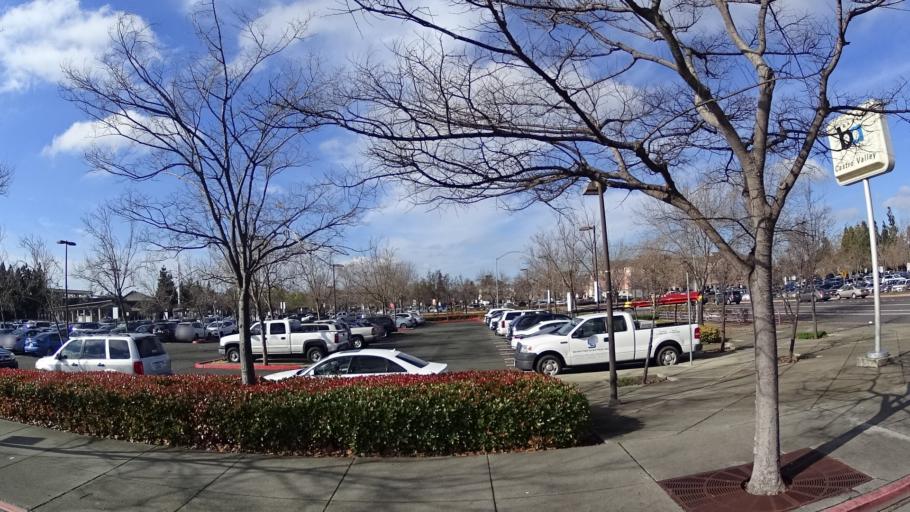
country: US
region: California
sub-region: Alameda County
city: Castro Valley
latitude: 37.6923
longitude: -122.0740
